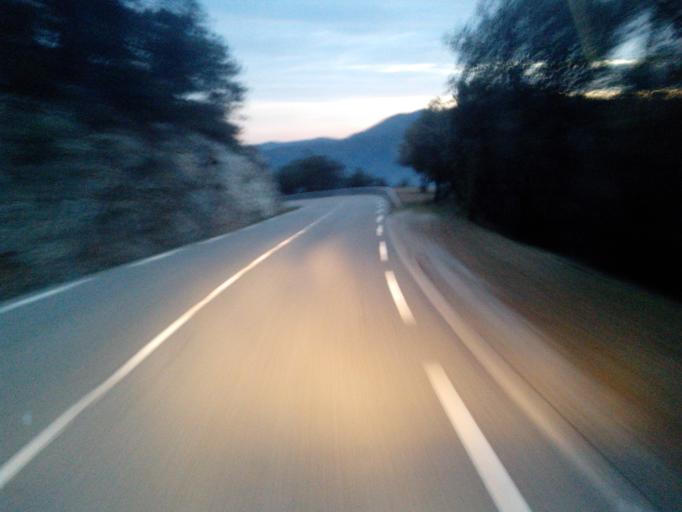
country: FR
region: Languedoc-Roussillon
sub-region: Departement du Gard
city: Saint-Jean-du-Gard
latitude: 44.1343
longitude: 3.8468
